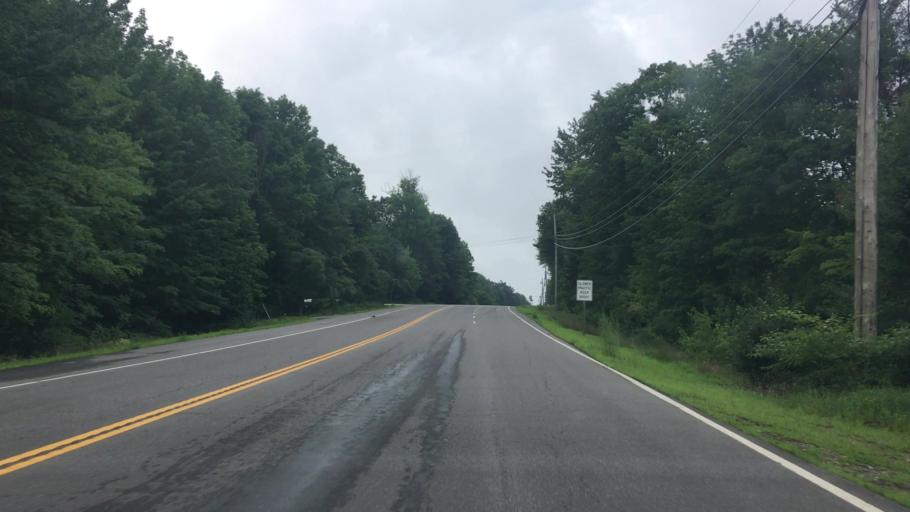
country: US
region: Maine
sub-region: York County
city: Sanford (historical)
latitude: 43.4268
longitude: -70.8115
